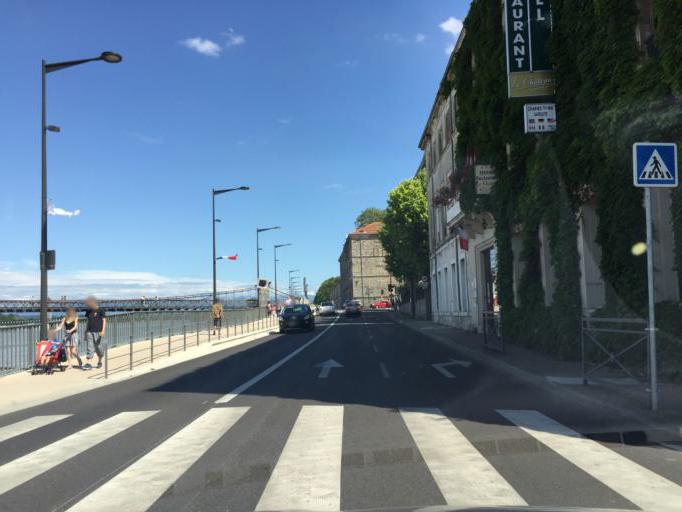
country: FR
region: Rhone-Alpes
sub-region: Departement de l'Ardeche
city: Tournon-sur-Rhone
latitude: 45.0683
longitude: 4.8335
